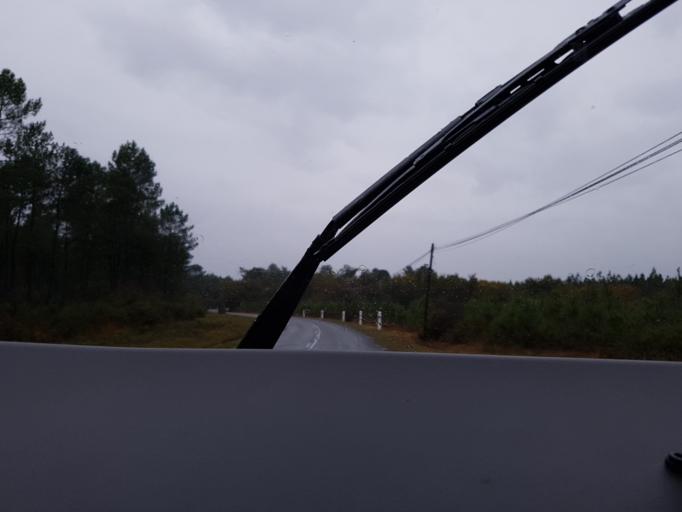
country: FR
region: Aquitaine
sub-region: Departement de la Gironde
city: Saint-Symphorien
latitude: 44.3439
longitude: -0.6094
